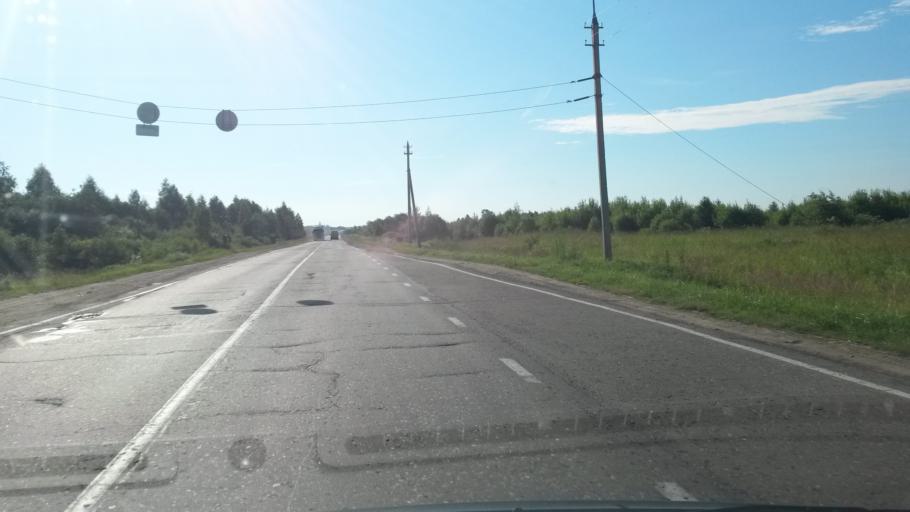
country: RU
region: Jaroslavl
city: Dubki
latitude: 57.2437
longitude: 40.1533
